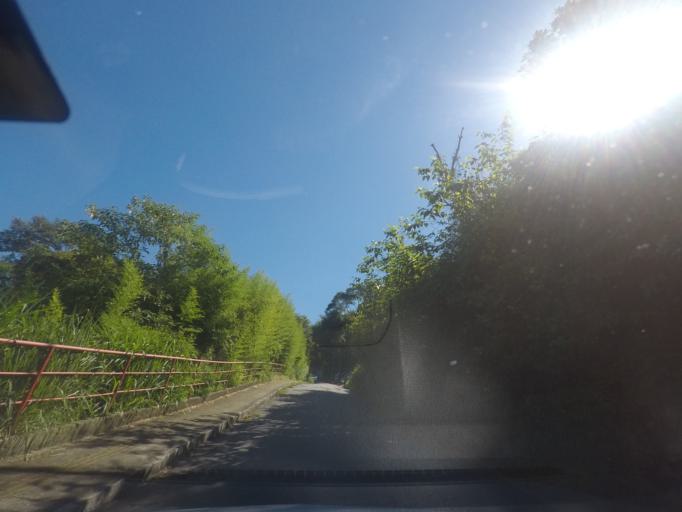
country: BR
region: Rio de Janeiro
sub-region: Petropolis
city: Petropolis
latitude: -22.5113
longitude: -43.1879
